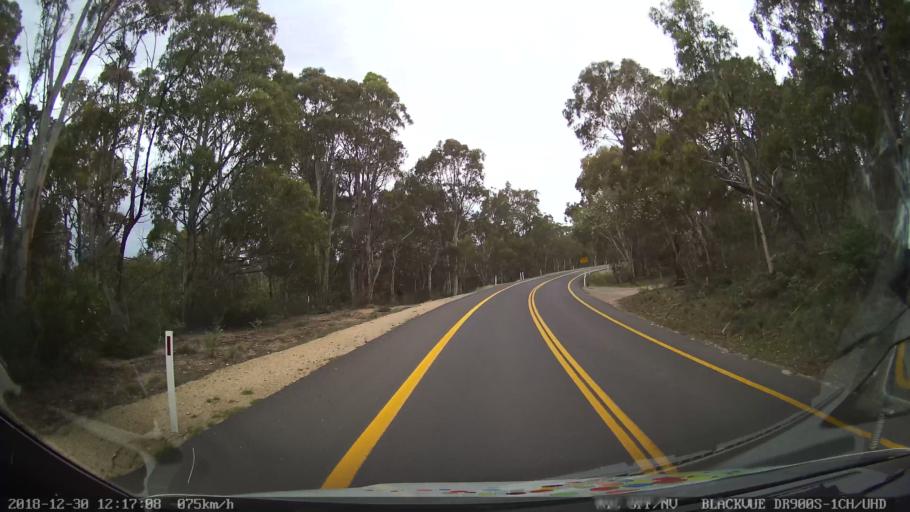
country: AU
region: New South Wales
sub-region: Snowy River
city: Jindabyne
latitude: -36.3521
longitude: 148.5636
